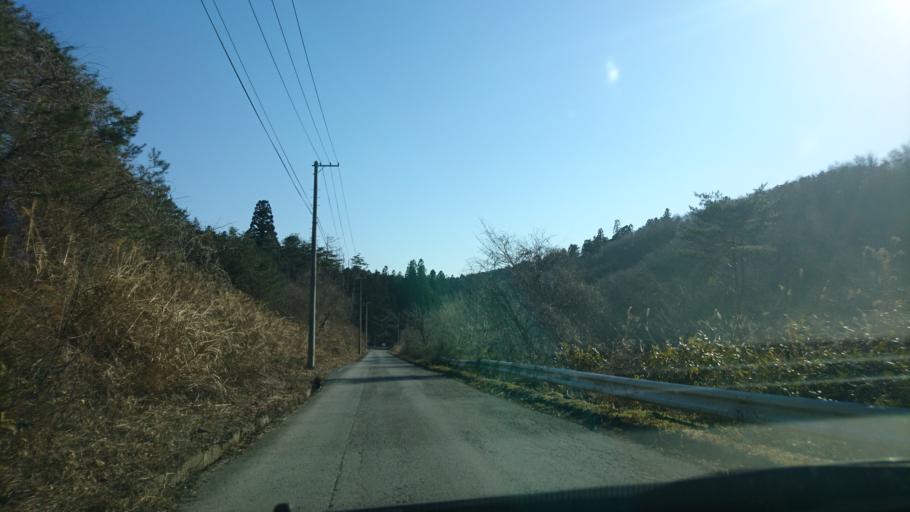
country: JP
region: Iwate
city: Ichinoseki
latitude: 38.8047
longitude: 141.2652
